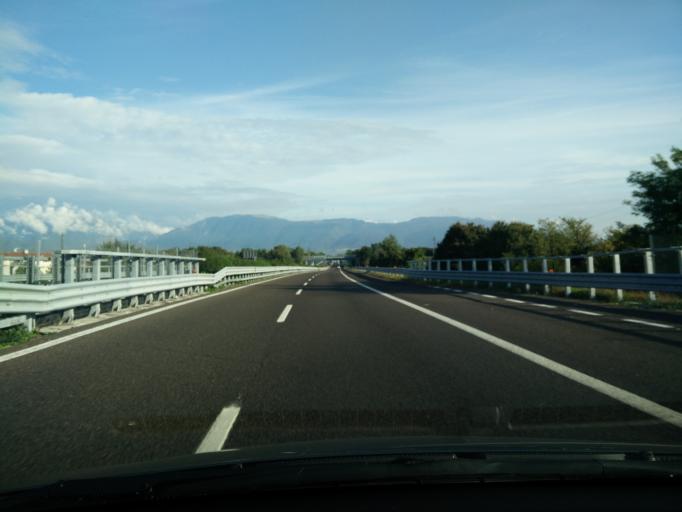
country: IT
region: Veneto
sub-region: Provincia di Treviso
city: San Vendemiano
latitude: 45.8886
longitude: 12.3412
